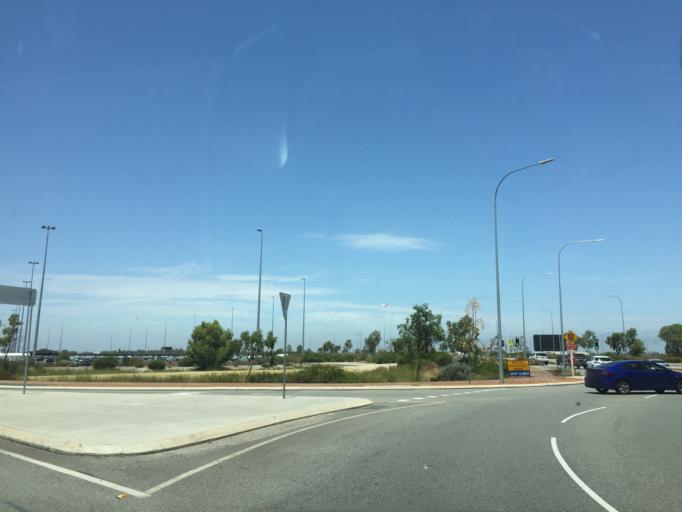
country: AU
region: Western Australia
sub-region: Belmont
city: Redcliffe
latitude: -31.9485
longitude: 115.9728
